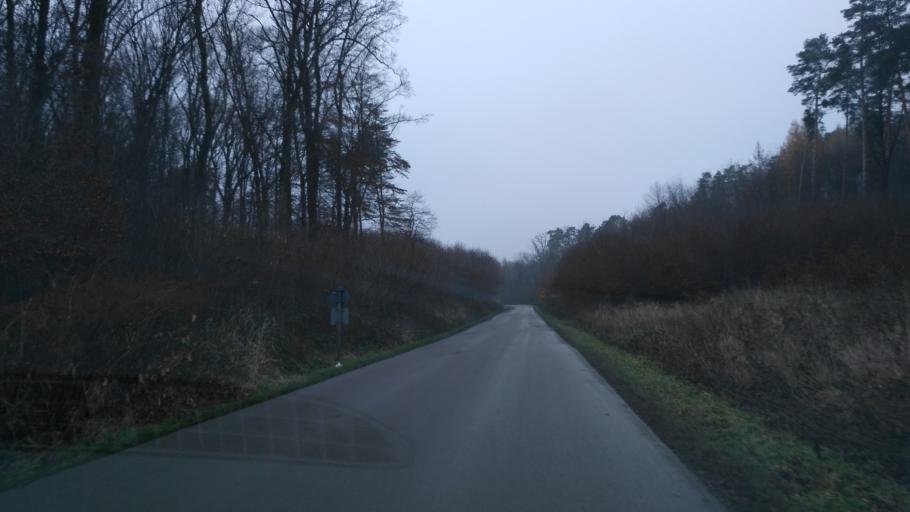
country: PL
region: Subcarpathian Voivodeship
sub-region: Powiat przeworski
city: Zarzecze
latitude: 49.9958
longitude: 22.5165
